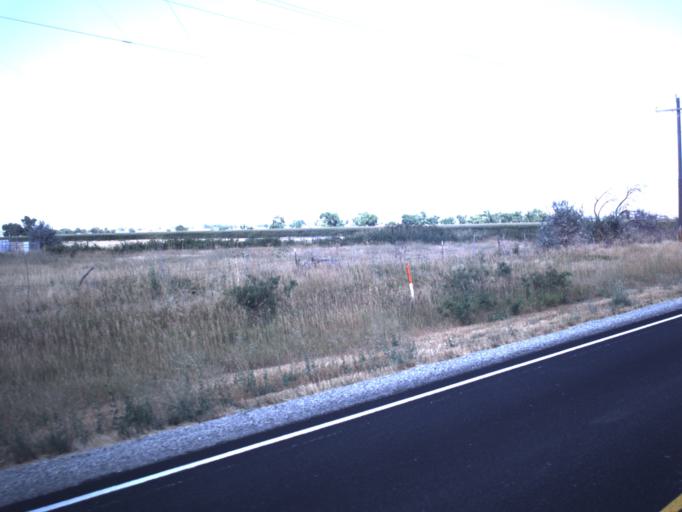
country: US
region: Utah
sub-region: Box Elder County
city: Honeyville
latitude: 41.6360
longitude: -112.1285
